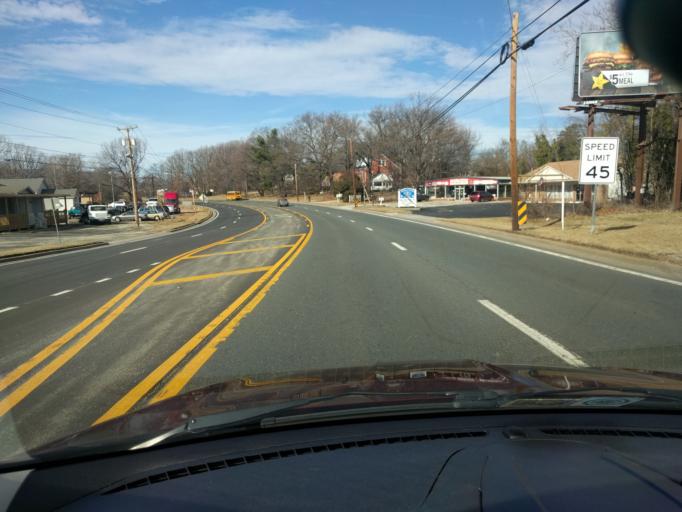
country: US
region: Virginia
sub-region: Amherst County
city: Madison Heights
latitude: 37.4834
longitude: -79.1190
